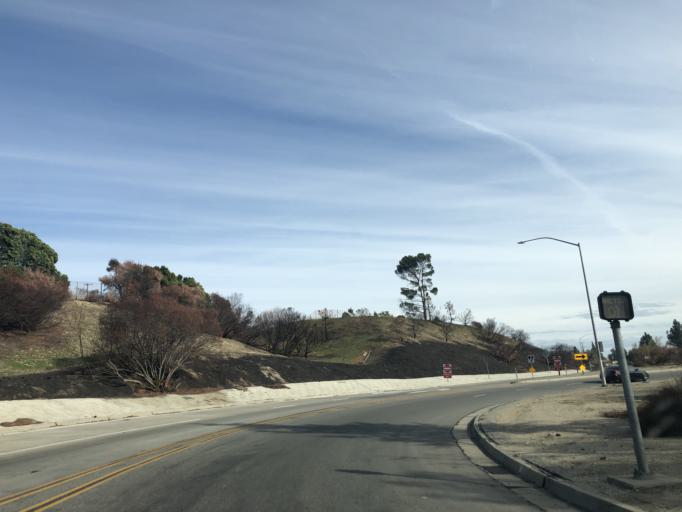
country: US
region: California
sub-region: Los Angeles County
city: San Fernando
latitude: 34.3241
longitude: -118.4792
